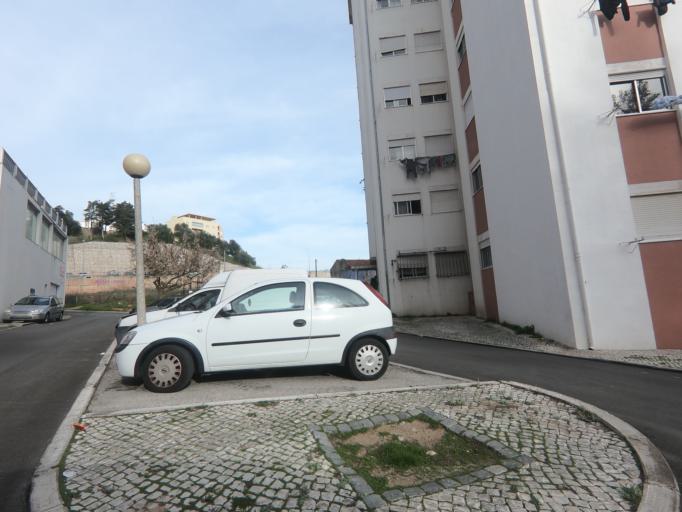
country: PT
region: Setubal
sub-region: Setubal
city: Setubal
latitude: 38.5227
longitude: -8.9047
